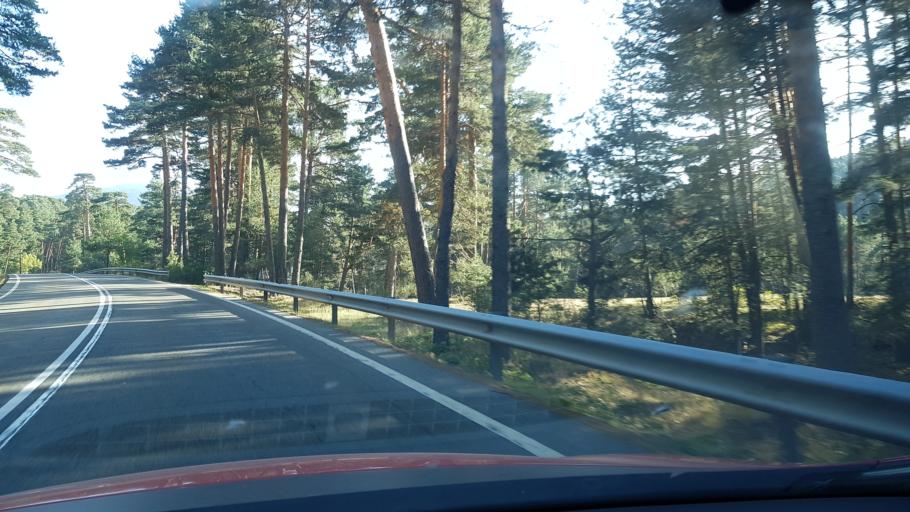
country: ES
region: Castille and Leon
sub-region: Provincia de Segovia
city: San Ildefonso
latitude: 40.8335
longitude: -4.0244
